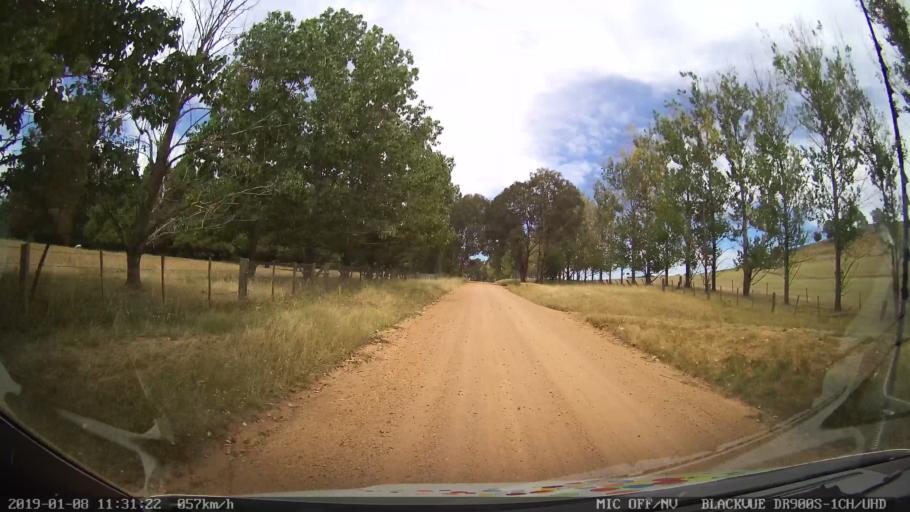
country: AU
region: New South Wales
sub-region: Guyra
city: Guyra
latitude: -30.3121
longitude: 151.5376
